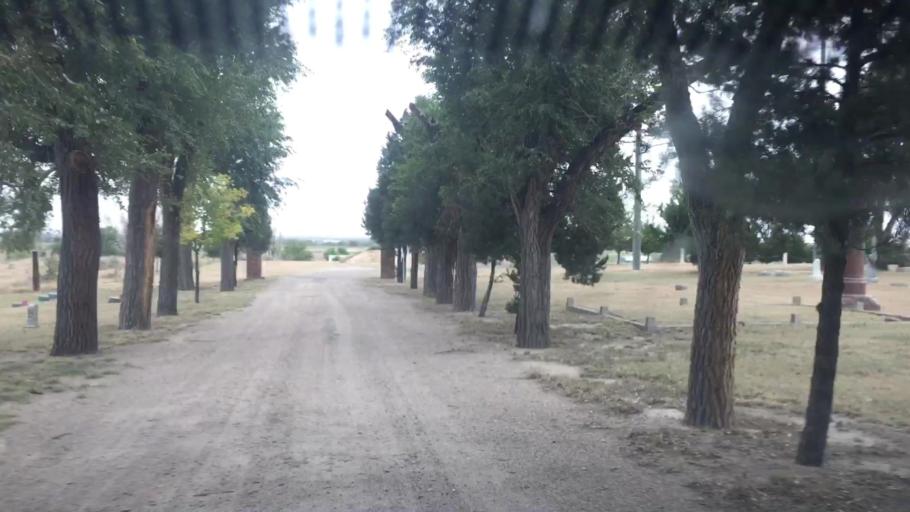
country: US
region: Kansas
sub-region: Hamilton County
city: Syracuse
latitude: 38.0586
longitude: -102.1088
